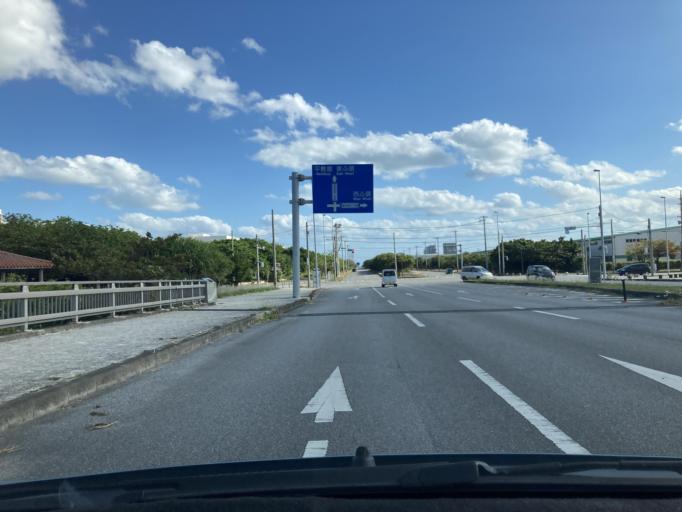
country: JP
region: Okinawa
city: Katsuren-haebaru
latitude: 26.3423
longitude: 127.8572
